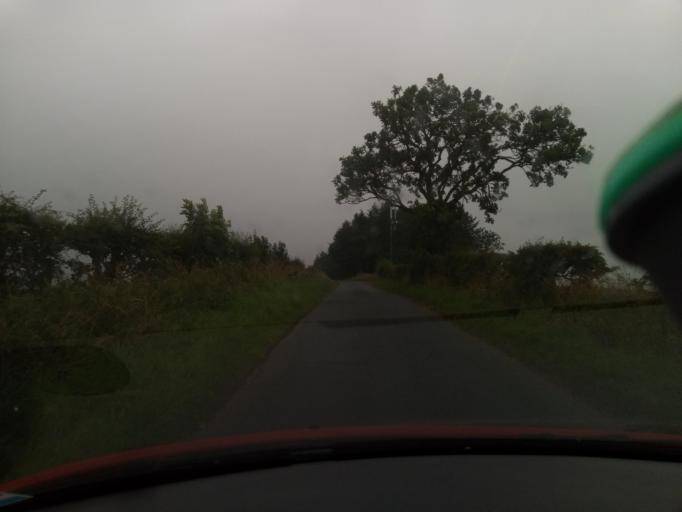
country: GB
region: Scotland
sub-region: The Scottish Borders
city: Earlston
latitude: 55.6488
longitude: -2.7066
